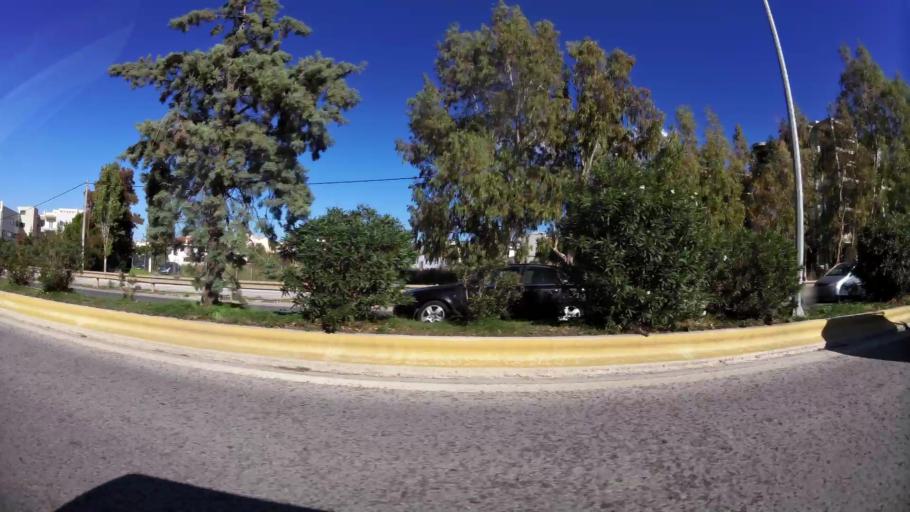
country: GR
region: Attica
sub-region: Nomarchia Anatolikis Attikis
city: Markopoulo
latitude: 37.8774
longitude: 23.9291
